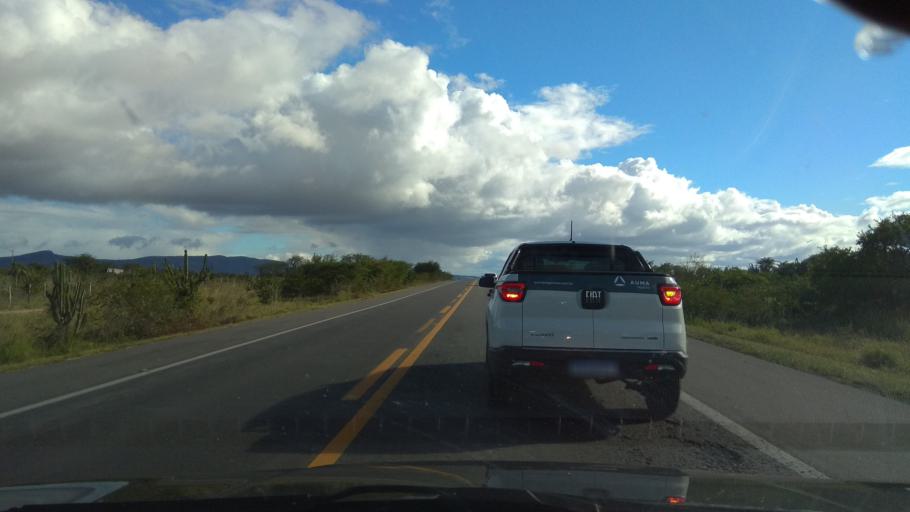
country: BR
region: Bahia
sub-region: Castro Alves
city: Castro Alves
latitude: -12.6773
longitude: -39.6641
